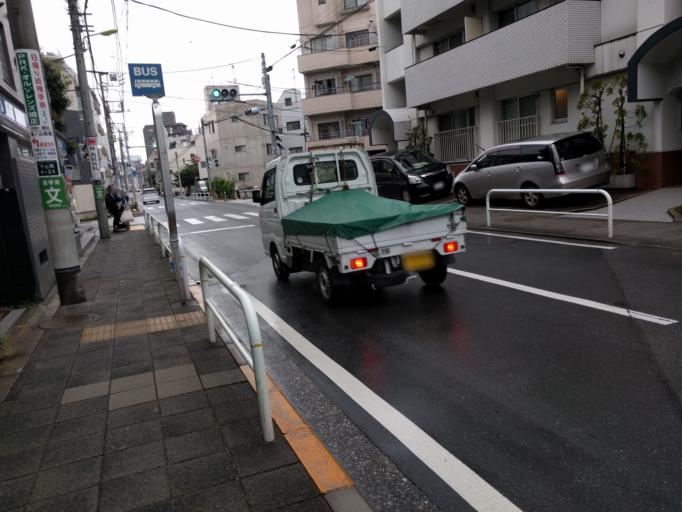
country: JP
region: Tokyo
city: Tokyo
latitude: 35.6368
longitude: 139.6817
